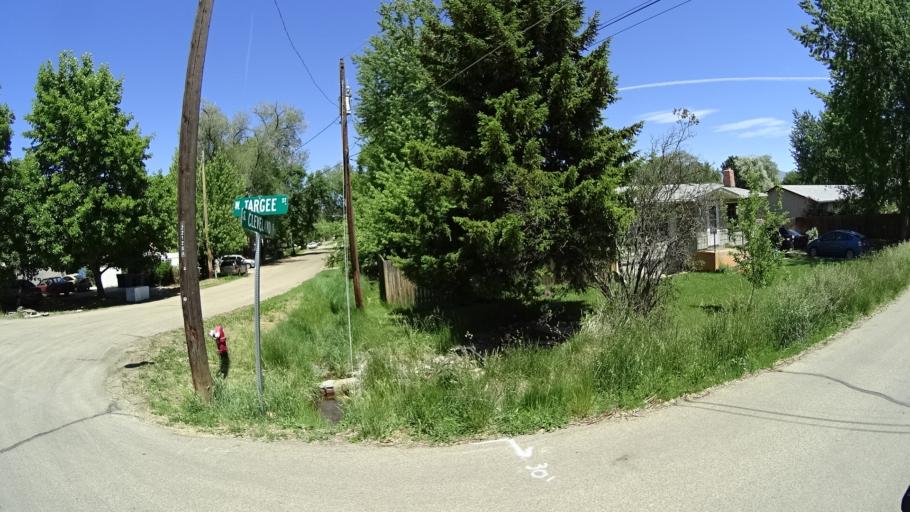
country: US
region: Idaho
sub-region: Ada County
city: Garden City
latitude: 43.5825
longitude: -116.2311
